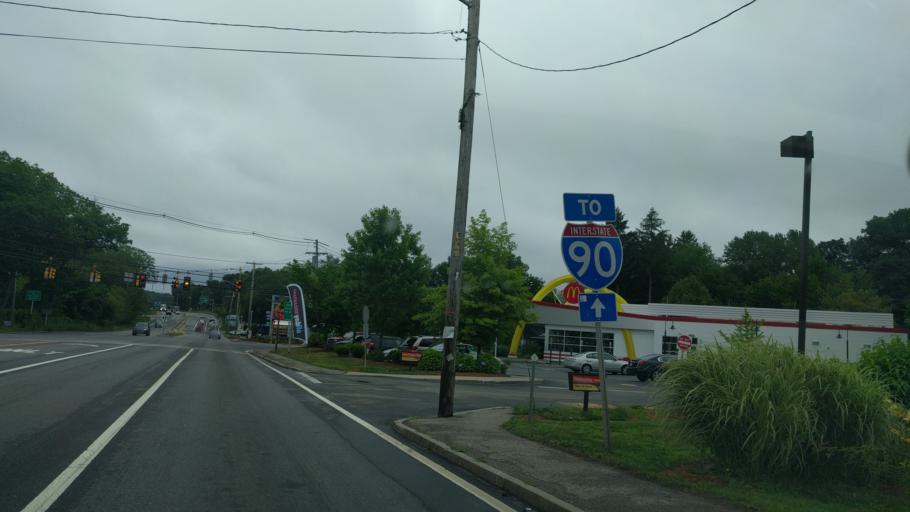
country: US
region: Massachusetts
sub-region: Worcester County
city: Millbury
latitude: 42.2118
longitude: -71.7963
